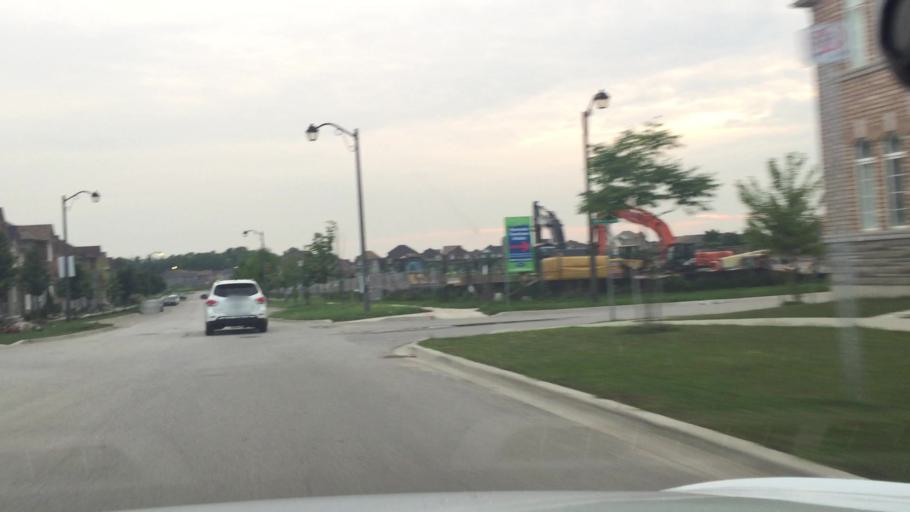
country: CA
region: Ontario
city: Markham
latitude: 43.8889
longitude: -79.2152
